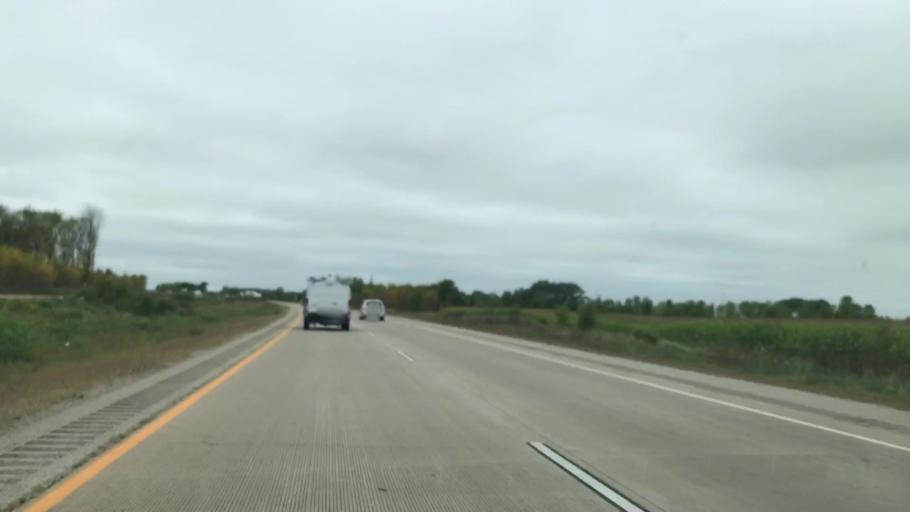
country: US
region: Wisconsin
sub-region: Marinette County
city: Peshtigo
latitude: 45.0404
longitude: -87.8220
